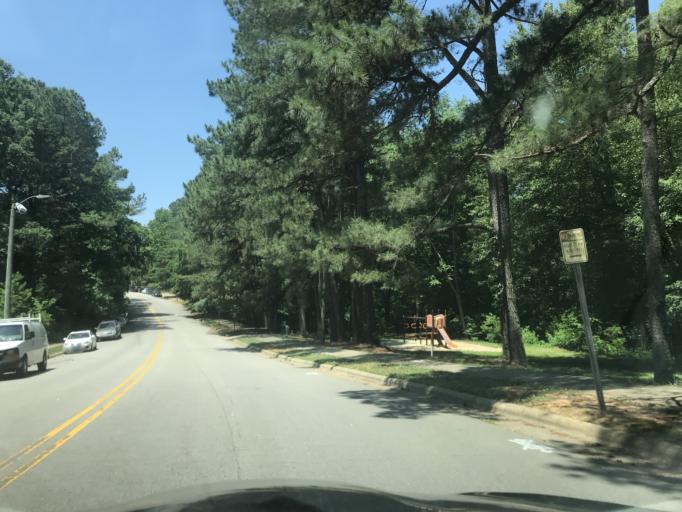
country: US
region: North Carolina
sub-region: Wake County
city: West Raleigh
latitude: 35.8629
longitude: -78.6512
